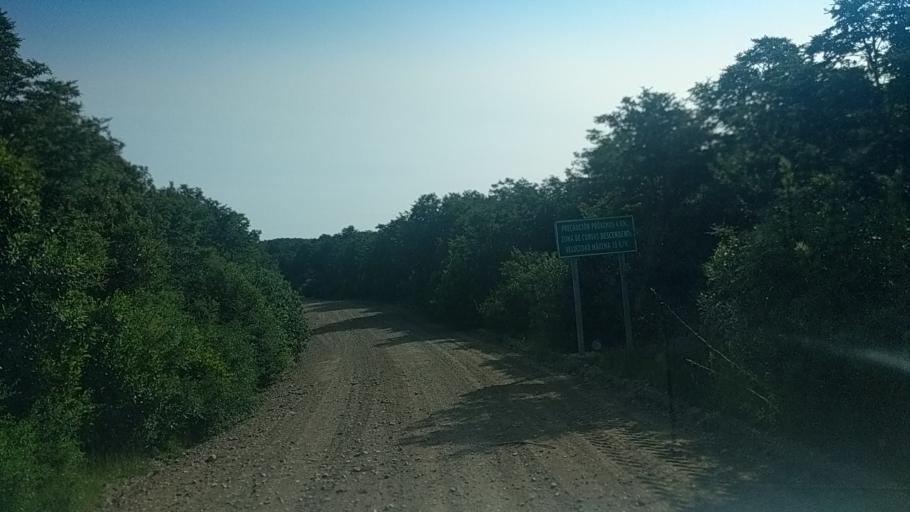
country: AR
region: Chubut
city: Rio Pico
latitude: -44.2475
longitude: -71.8057
